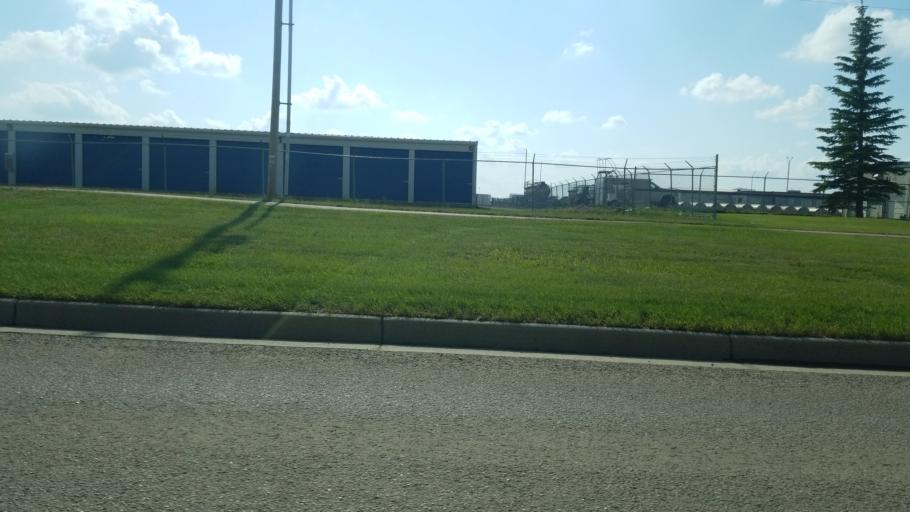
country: CA
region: Saskatchewan
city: Lloydminster
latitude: 53.2888
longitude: -110.0340
